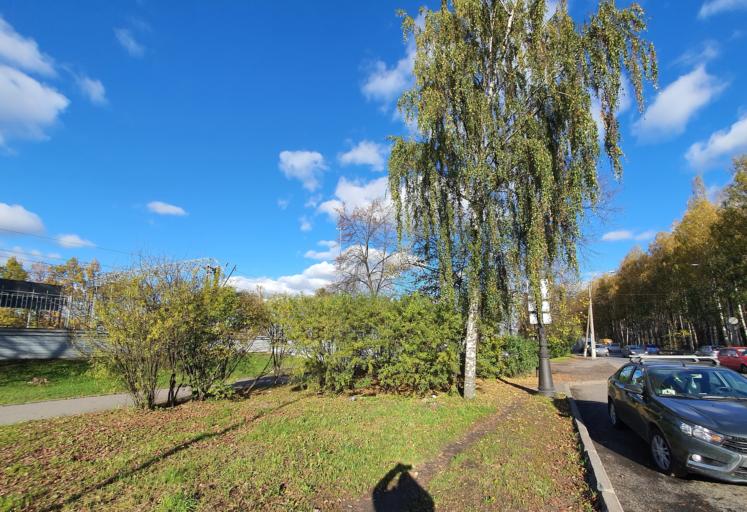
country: RU
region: St.-Petersburg
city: Pavlovsk
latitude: 59.6936
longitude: 30.4339
